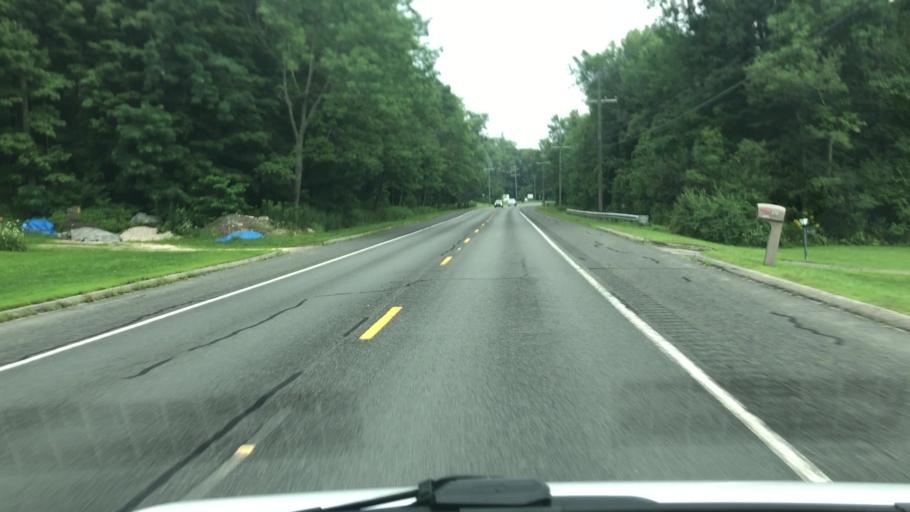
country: US
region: Massachusetts
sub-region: Berkshire County
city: Lanesborough
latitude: 42.5707
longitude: -73.2485
